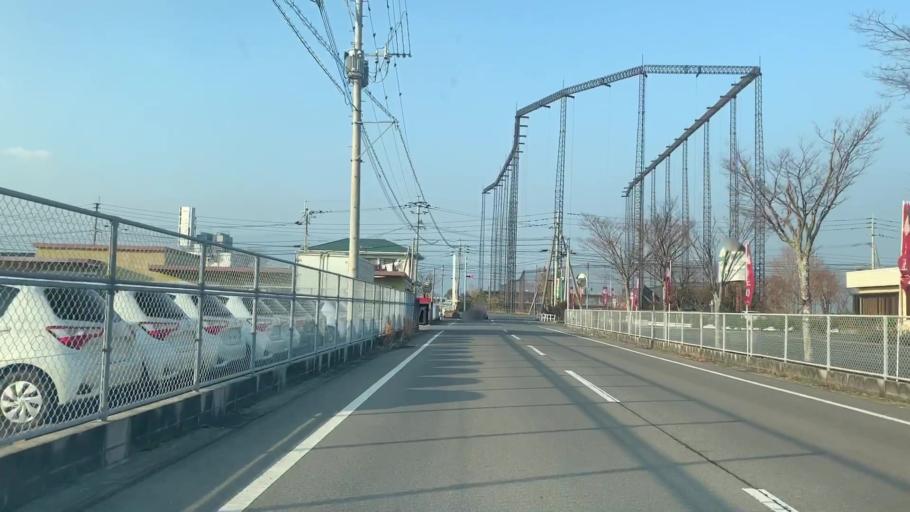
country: JP
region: Saga Prefecture
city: Saga-shi
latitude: 33.2643
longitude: 130.2478
